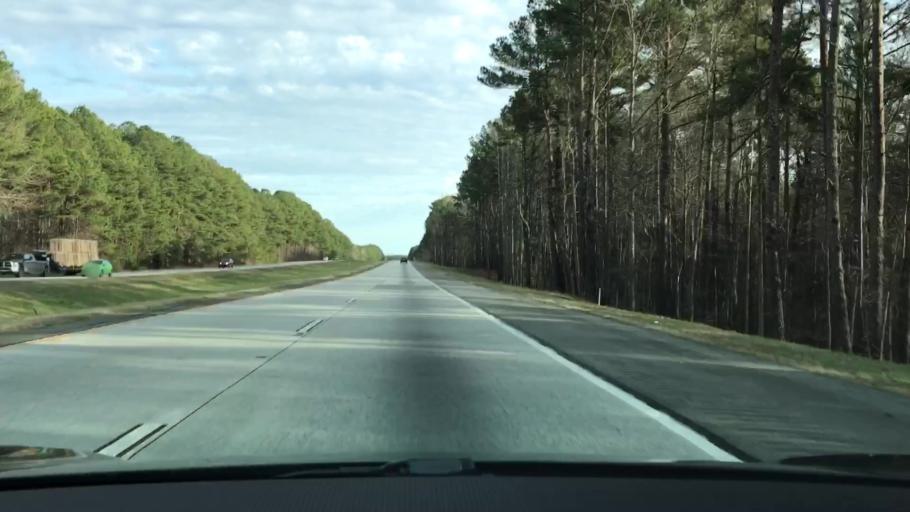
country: US
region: Georgia
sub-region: Taliaferro County
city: Crawfordville
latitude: 33.5079
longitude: -82.8385
